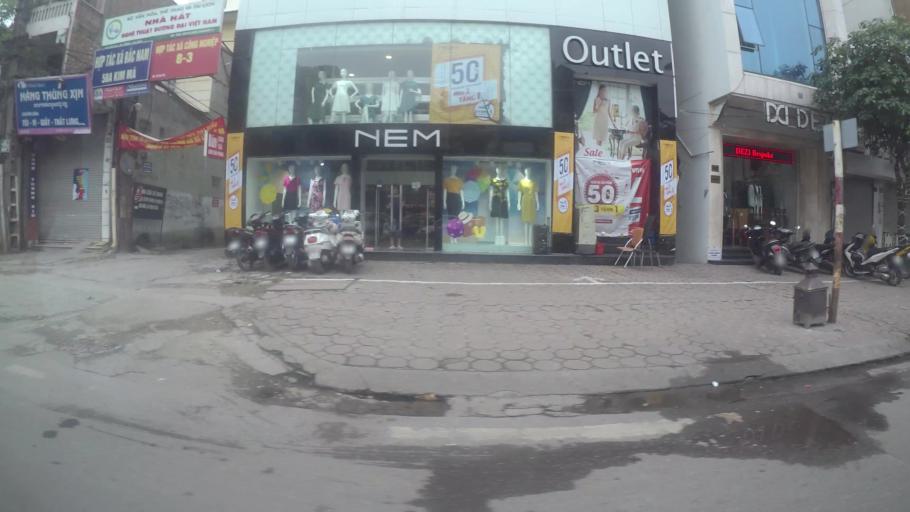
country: VN
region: Ha Noi
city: Dong Da
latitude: 21.0325
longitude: 105.8283
